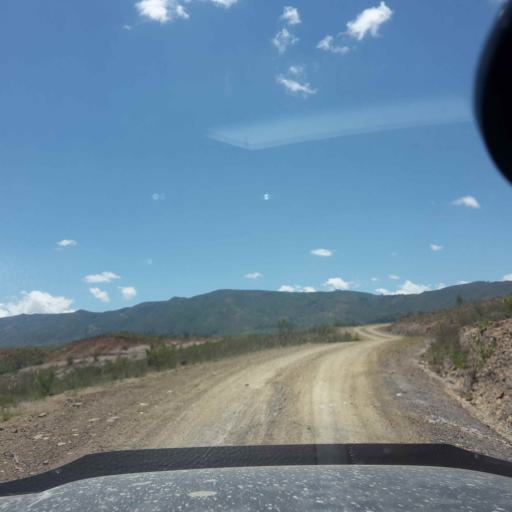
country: BO
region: Cochabamba
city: Totora
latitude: -17.7731
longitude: -65.2683
